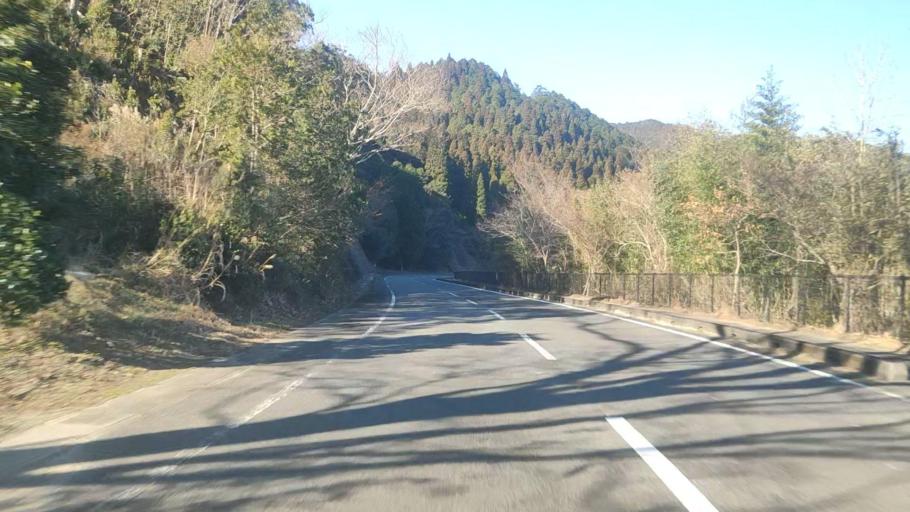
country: JP
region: Miyazaki
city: Nobeoka
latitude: 32.7474
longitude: 131.8069
